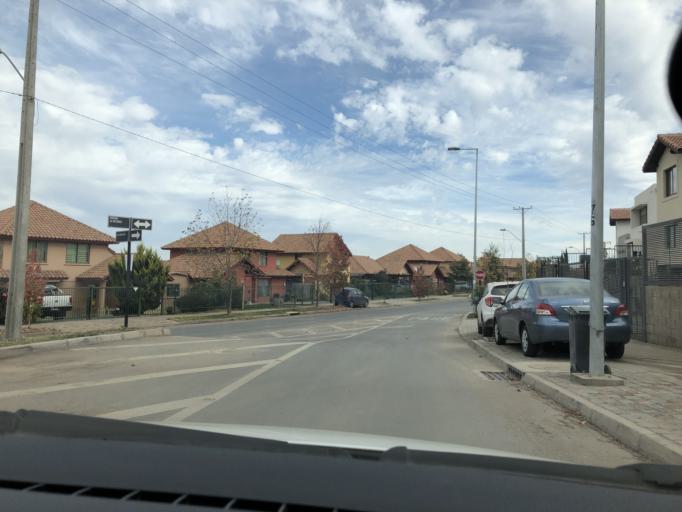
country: CL
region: Santiago Metropolitan
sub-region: Provincia de Cordillera
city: Puente Alto
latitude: -33.5819
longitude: -70.5095
